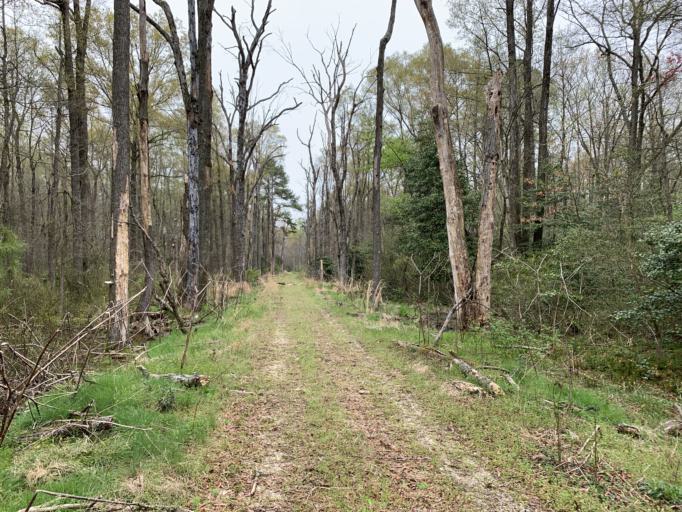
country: US
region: Delaware
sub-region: Kent County
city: Felton
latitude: 39.0233
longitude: -75.6342
